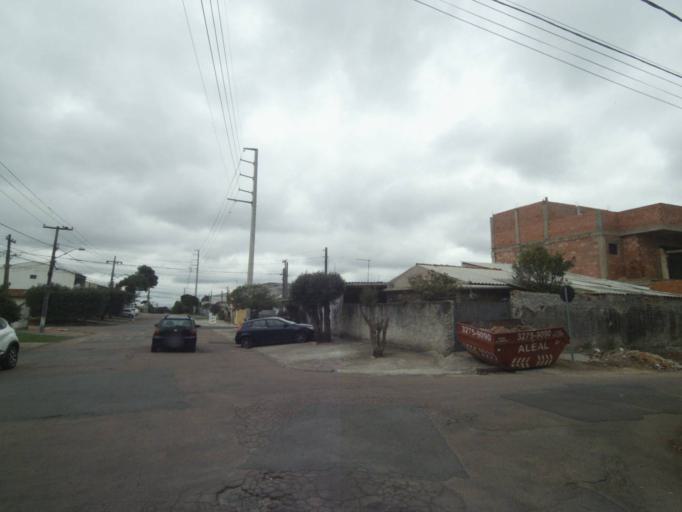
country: BR
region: Parana
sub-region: Sao Jose Dos Pinhais
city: Sao Jose dos Pinhais
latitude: -25.5428
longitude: -49.2837
